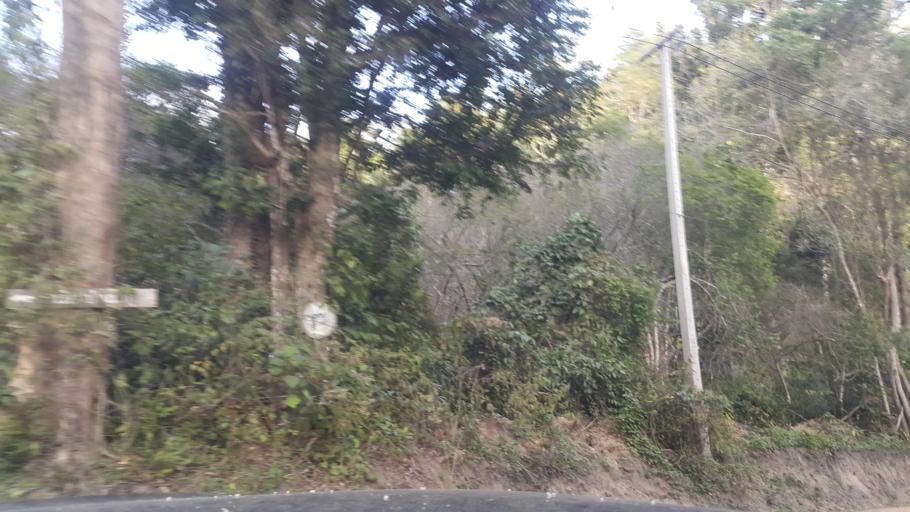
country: TH
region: Chiang Mai
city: Samoeng
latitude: 19.0067
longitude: 98.6476
